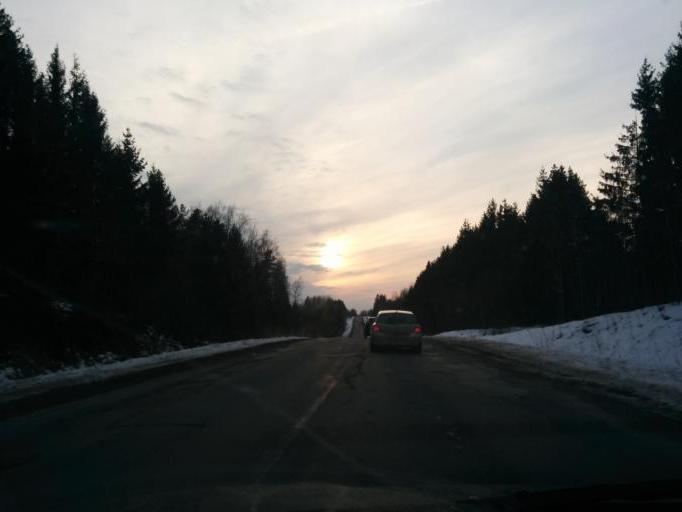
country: LV
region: Raunas
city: Rauna
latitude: 57.2834
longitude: 25.5107
